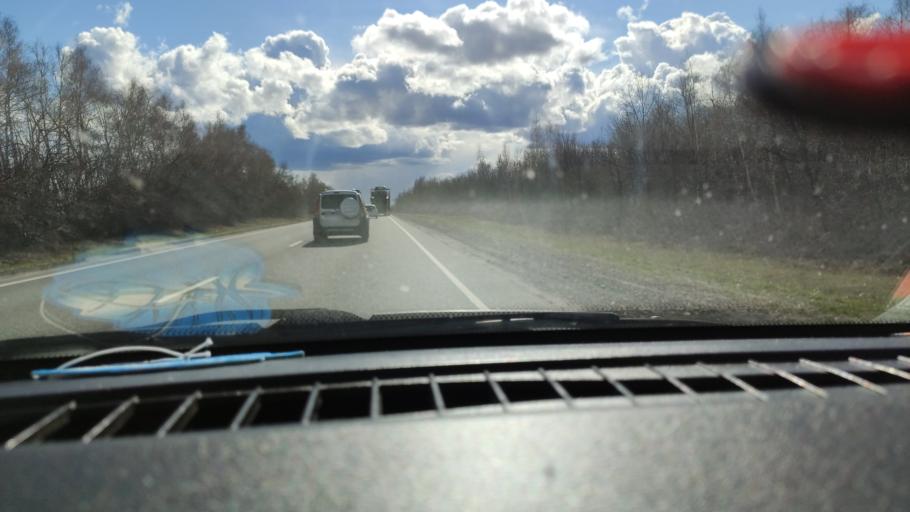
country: RU
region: Saratov
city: Khvalynsk
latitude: 52.5995
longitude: 48.1426
